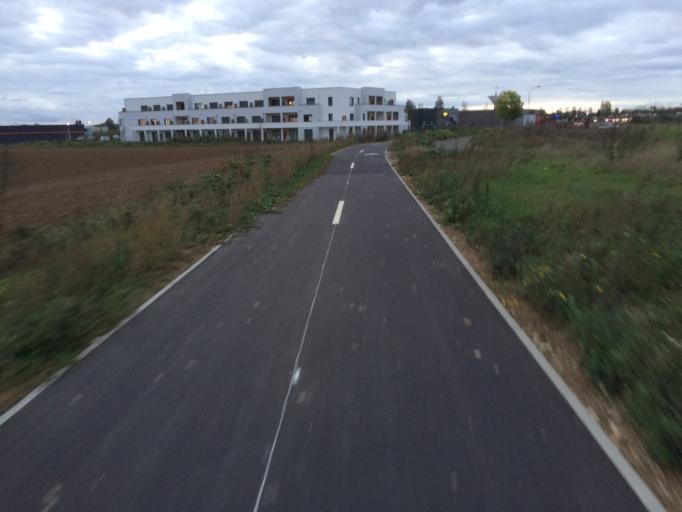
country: FR
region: Ile-de-France
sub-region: Departement de l'Essonne
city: Villejust
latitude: 48.6839
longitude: 2.2258
